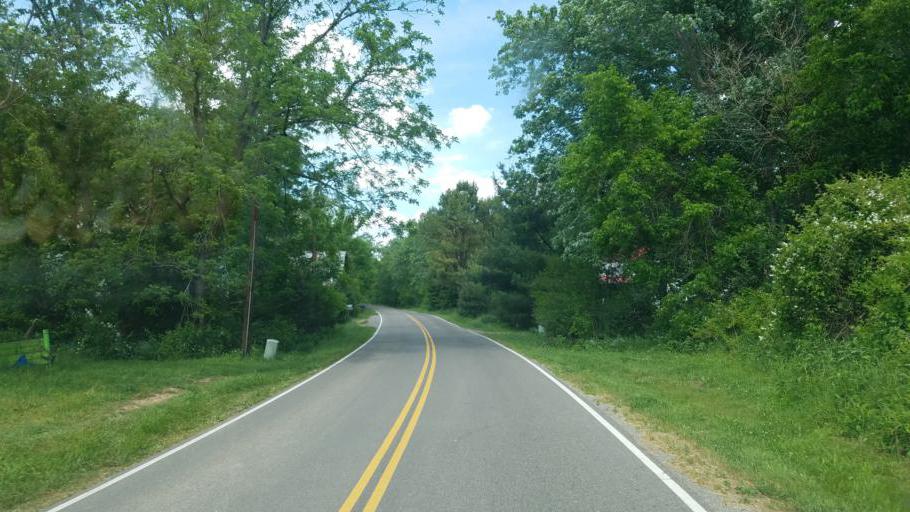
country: US
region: Ohio
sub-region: Meigs County
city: Pomeroy
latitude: 39.1019
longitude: -82.1322
